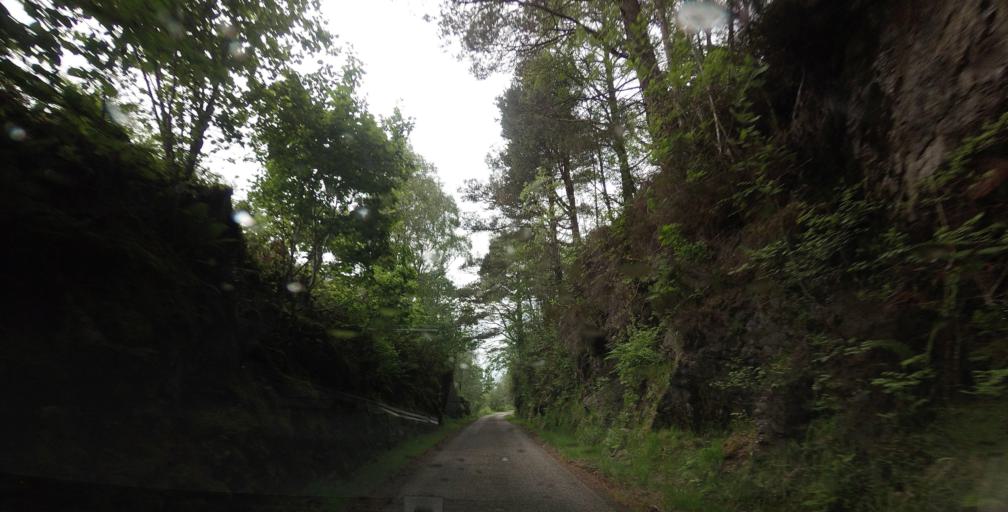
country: GB
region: Scotland
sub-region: Highland
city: Fort William
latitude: 56.7770
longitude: -5.1996
